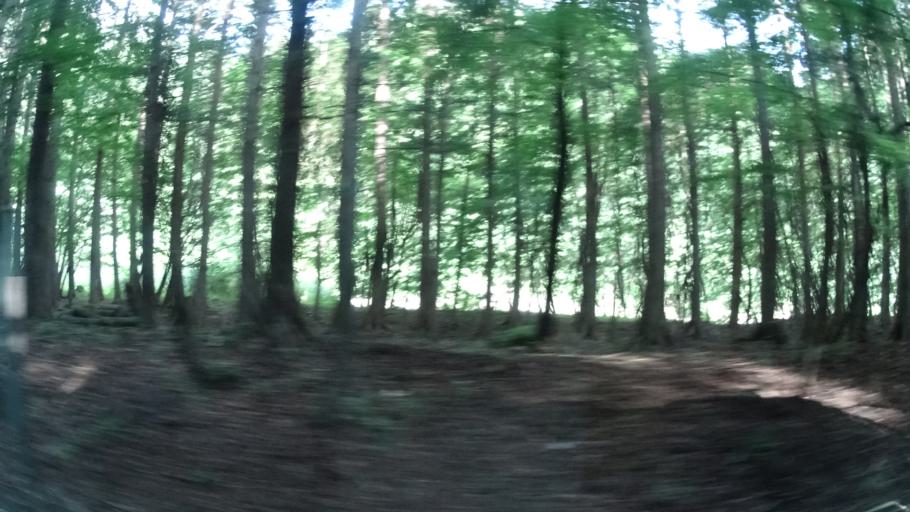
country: JP
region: Tochigi
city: Nikko
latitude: 36.6888
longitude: 139.4984
